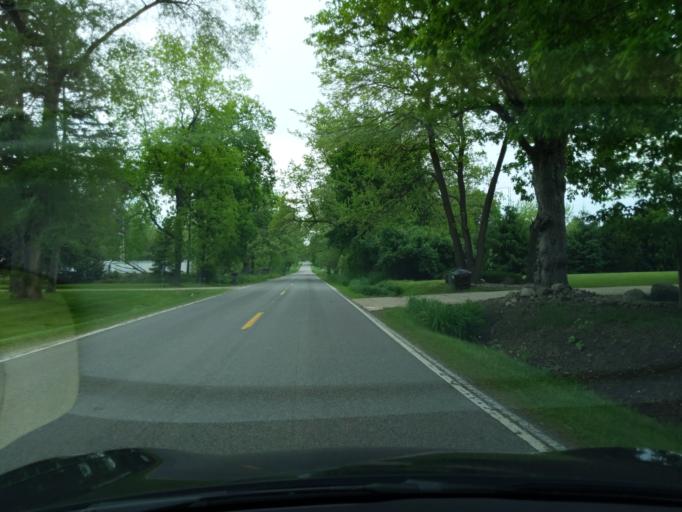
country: US
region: Michigan
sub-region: Ingham County
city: Leslie
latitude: 42.3663
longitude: -84.3490
